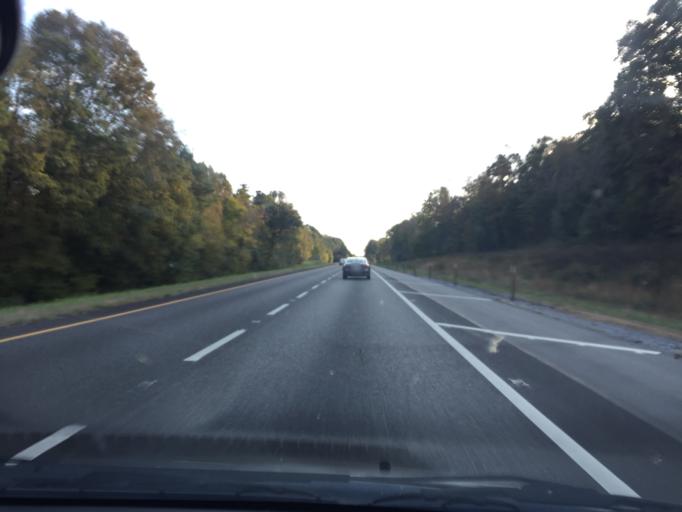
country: US
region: Tennessee
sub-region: Meigs County
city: Decatur
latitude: 35.3446
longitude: -84.7512
